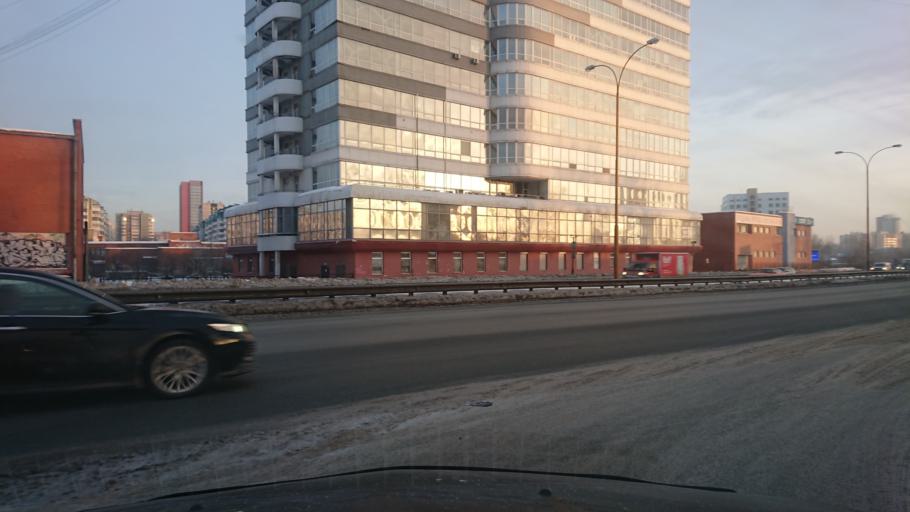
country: RU
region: Sverdlovsk
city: Yekaterinburg
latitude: 56.7871
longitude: 60.6297
